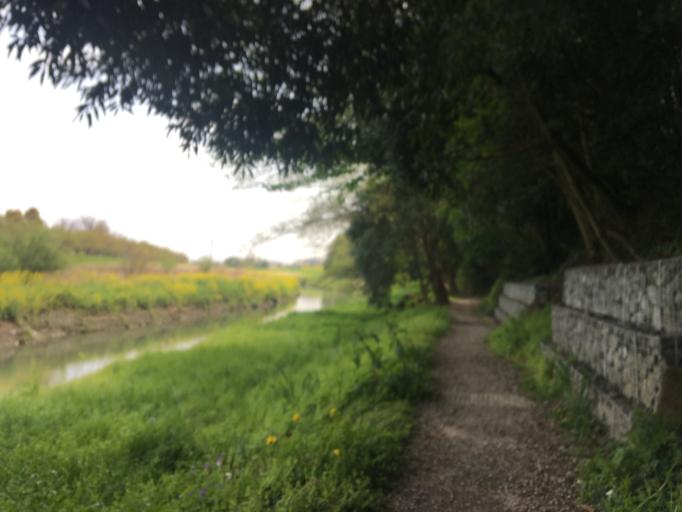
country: JP
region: Saitama
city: Kamifukuoka
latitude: 35.8821
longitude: 139.5261
